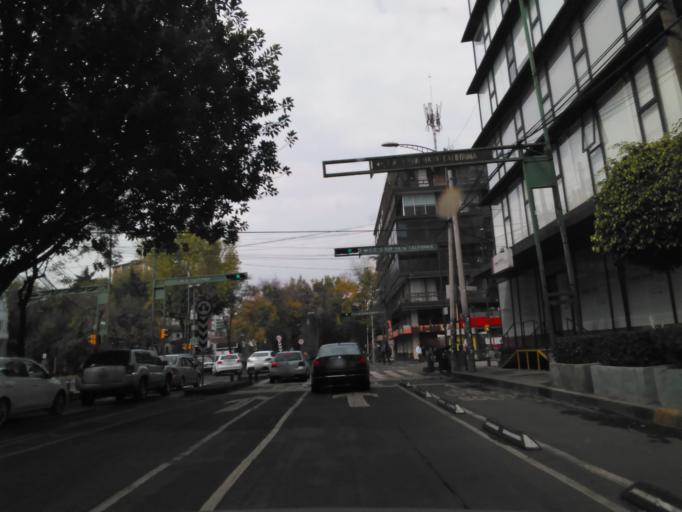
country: MX
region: Mexico City
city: Benito Juarez
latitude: 19.4054
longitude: -99.1716
